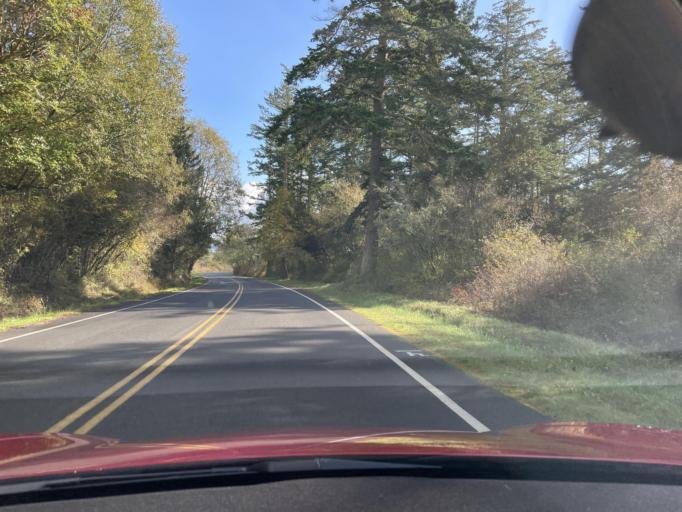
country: US
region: Washington
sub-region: San Juan County
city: Friday Harbor
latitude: 48.4685
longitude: -123.0117
